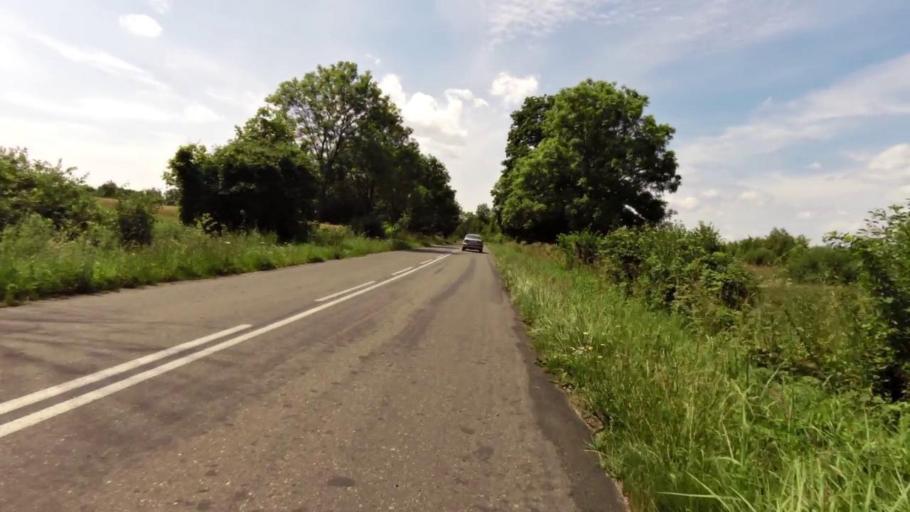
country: PL
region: West Pomeranian Voivodeship
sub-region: Powiat stargardzki
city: Marianowo
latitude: 53.3690
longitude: 15.3455
